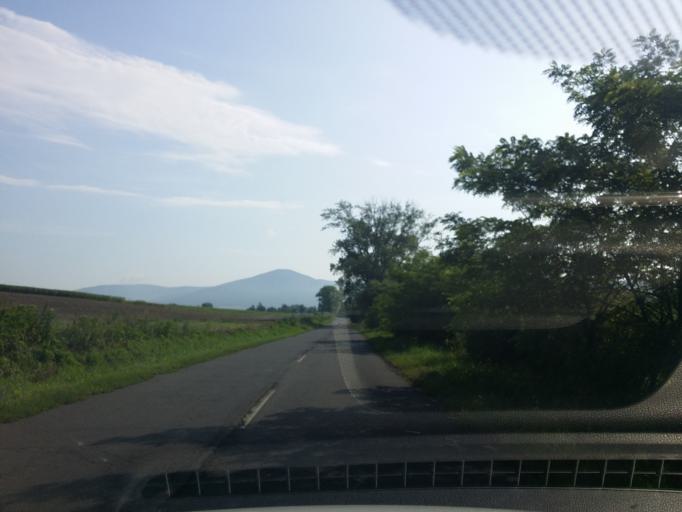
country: HU
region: Borsod-Abauj-Zemplen
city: Abaujszanto
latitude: 48.3732
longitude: 21.2337
